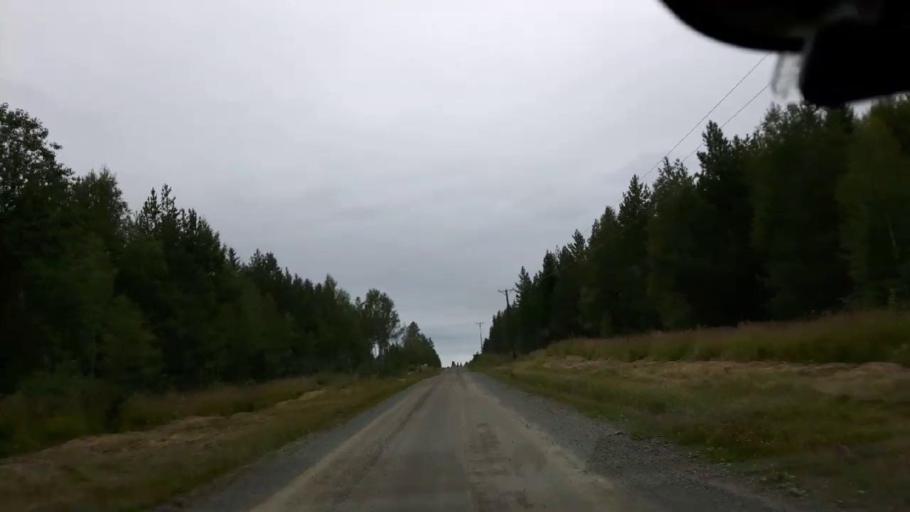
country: SE
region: Vaesternorrland
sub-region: Ange Kommun
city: Fransta
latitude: 62.8056
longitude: 16.0204
